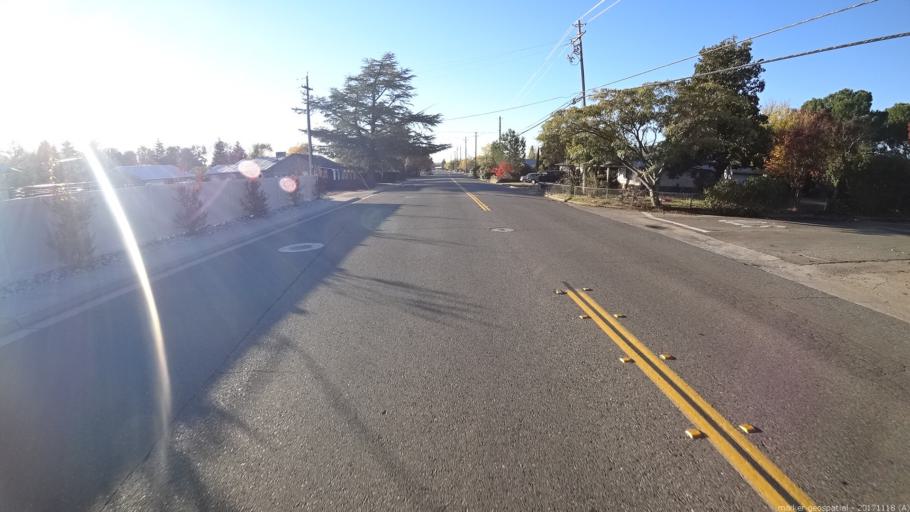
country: US
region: California
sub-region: Shasta County
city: Cottonwood
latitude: 40.3960
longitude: -122.2891
